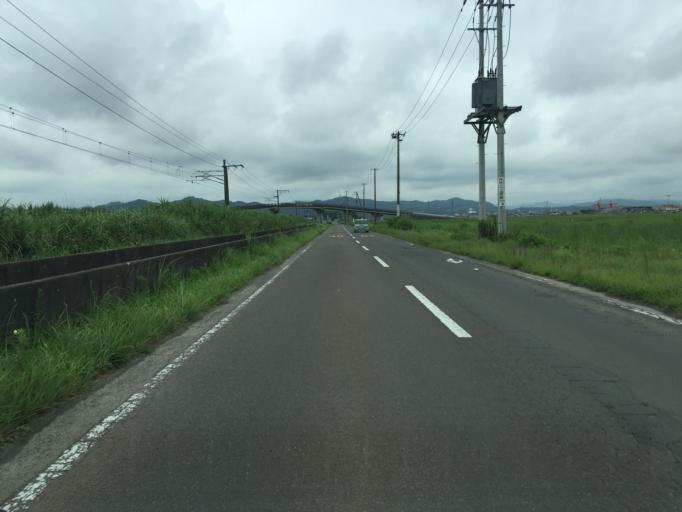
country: JP
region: Miyagi
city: Watari
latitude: 38.0245
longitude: 140.8780
